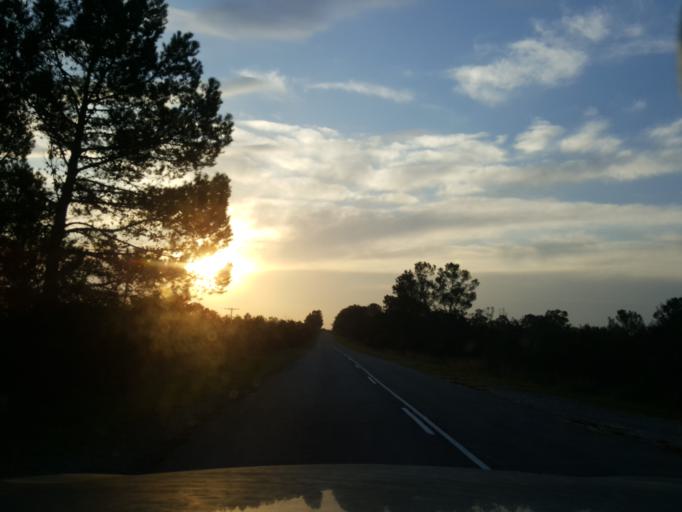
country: ZA
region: Eastern Cape
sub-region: Cacadu District Municipality
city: Grahamstown
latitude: -33.4567
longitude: 26.4966
